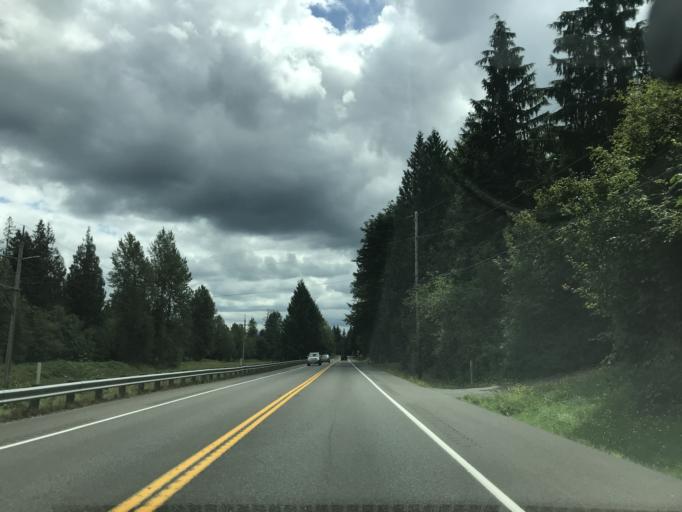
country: US
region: Washington
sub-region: King County
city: Maple Valley
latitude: 47.4083
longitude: -122.0525
